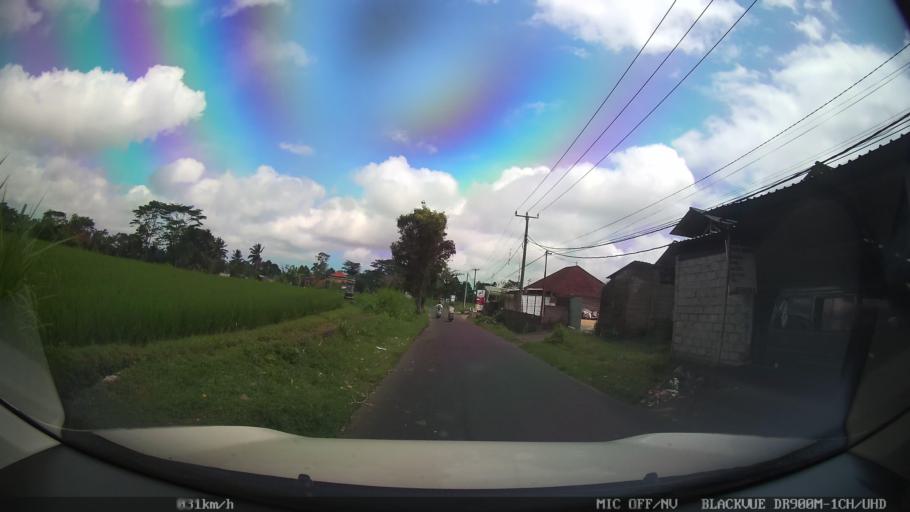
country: ID
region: Bali
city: Banjar Petak
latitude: -8.4529
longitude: 115.3184
